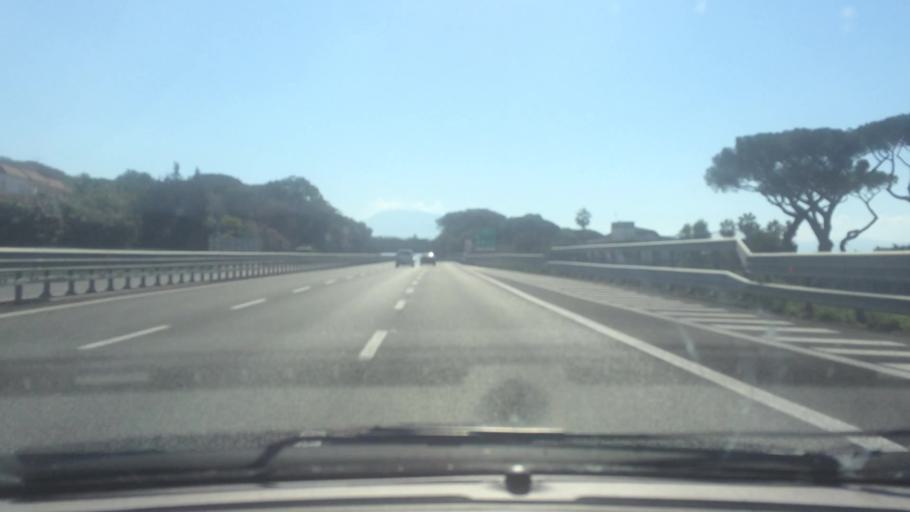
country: IT
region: Campania
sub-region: Provincia di Napoli
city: Ercolano
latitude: 40.7995
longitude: 14.3708
